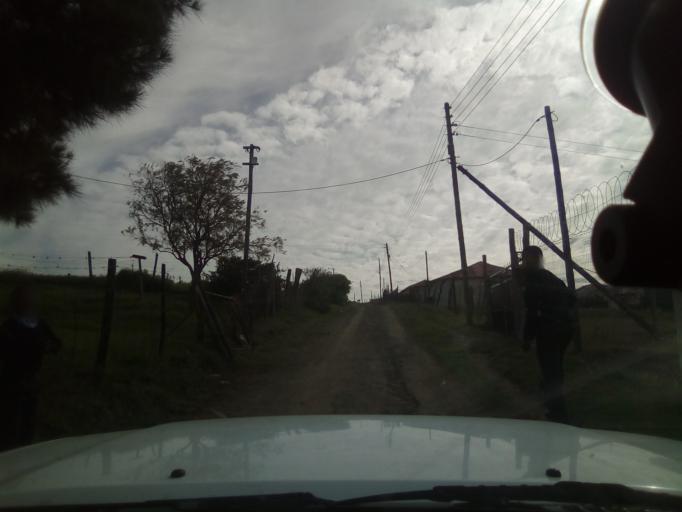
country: ZA
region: Eastern Cape
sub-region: Amathole District Municipality
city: Komga
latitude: -32.7933
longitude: 27.9623
